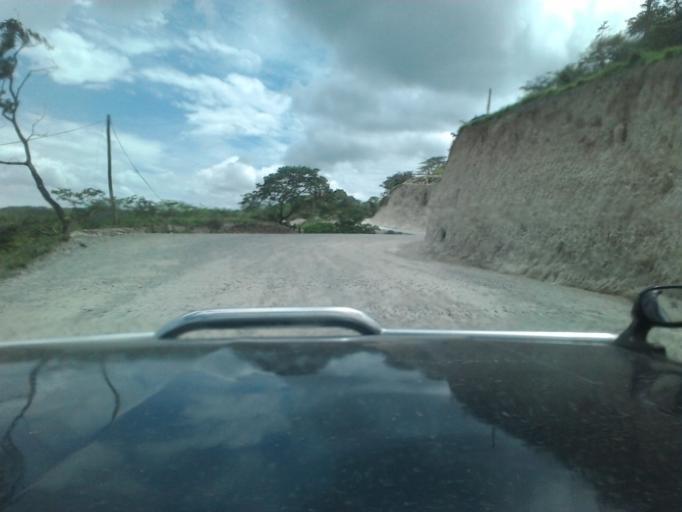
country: CR
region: Guanacaste
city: Juntas
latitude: 10.2563
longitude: -84.8408
